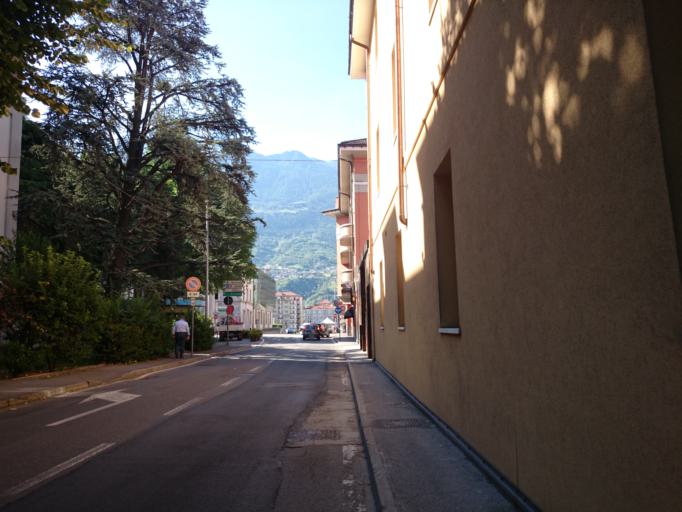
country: IT
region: Aosta Valley
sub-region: Valle d'Aosta
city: Aosta
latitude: 45.7356
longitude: 7.3127
